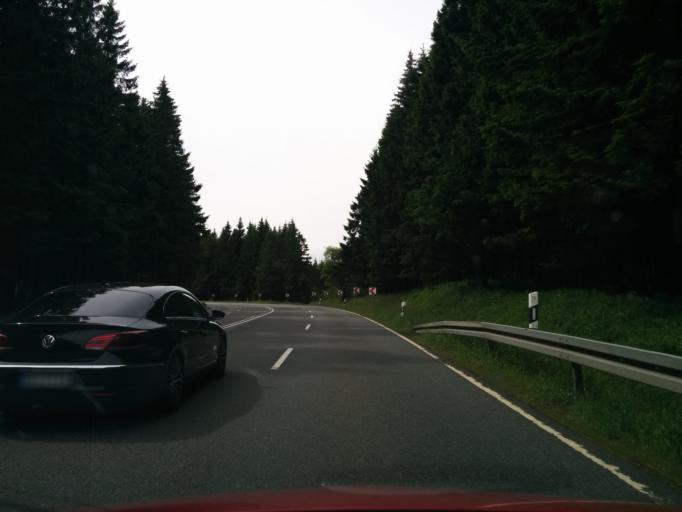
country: DE
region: Lower Saxony
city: Bad Harzburg
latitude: 51.8161
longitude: 10.5244
